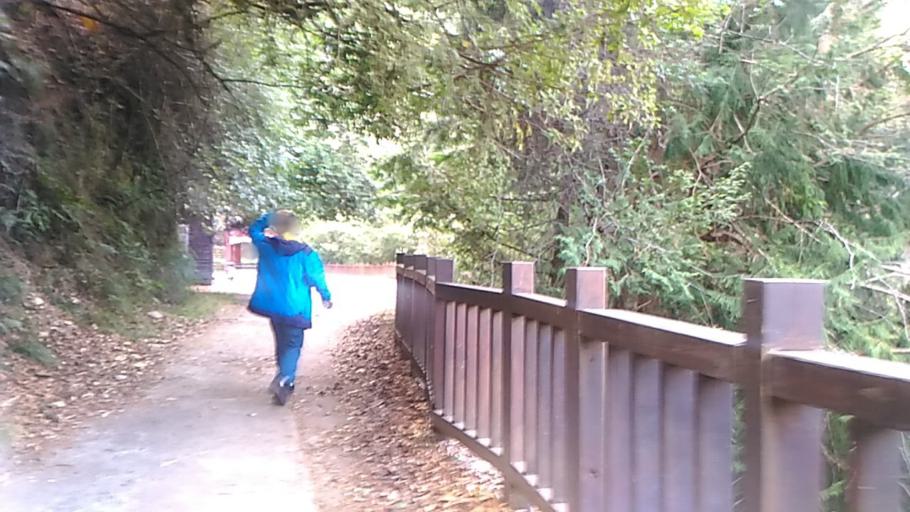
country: TW
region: Taiwan
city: Daxi
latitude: 24.4119
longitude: 121.3027
